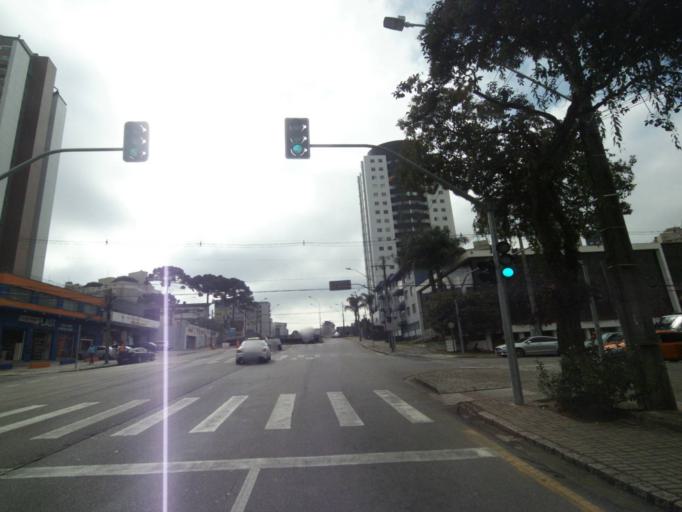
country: BR
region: Parana
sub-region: Curitiba
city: Curitiba
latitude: -25.4339
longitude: -49.2568
